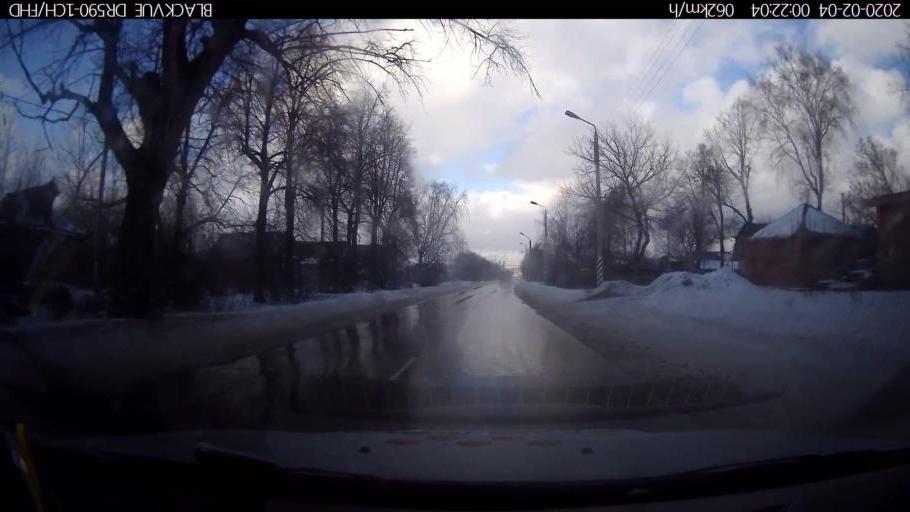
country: RU
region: Nizjnij Novgorod
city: Kstovo
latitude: 55.9682
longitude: 44.2100
